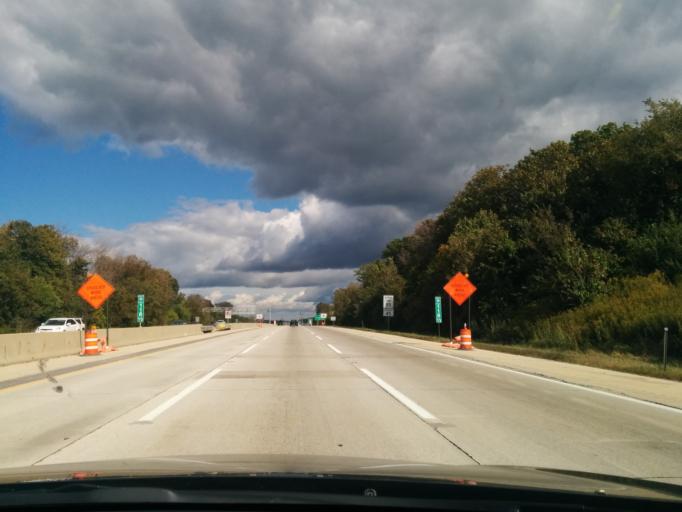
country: US
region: Illinois
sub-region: Kane County
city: North Aurora
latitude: 41.7975
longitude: -88.2970
